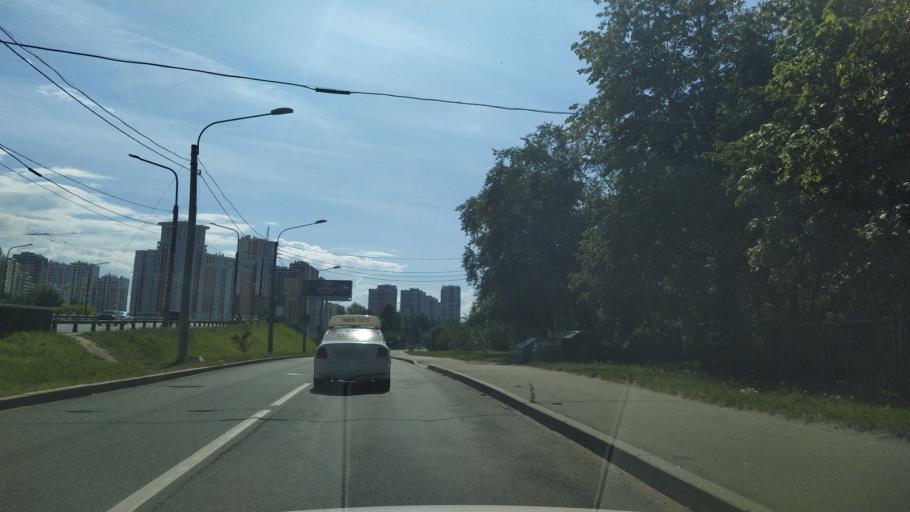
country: RU
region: Leningrad
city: Kalininskiy
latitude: 59.9940
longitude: 30.3780
